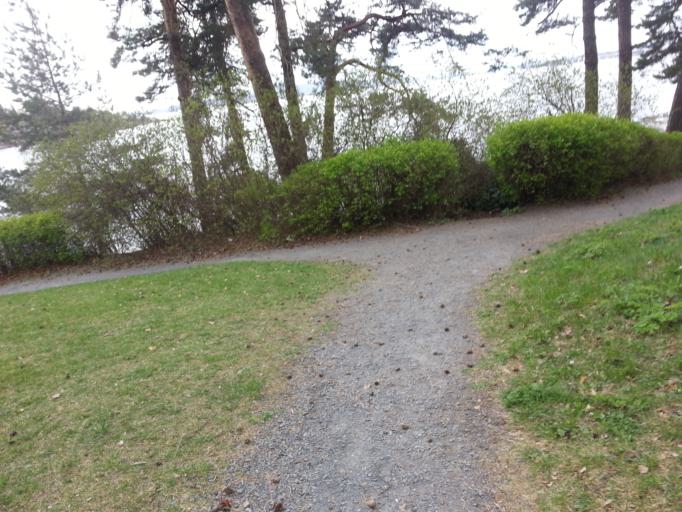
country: NO
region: Akershus
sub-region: Baerum
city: Lysaker
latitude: 59.9139
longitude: 10.6541
